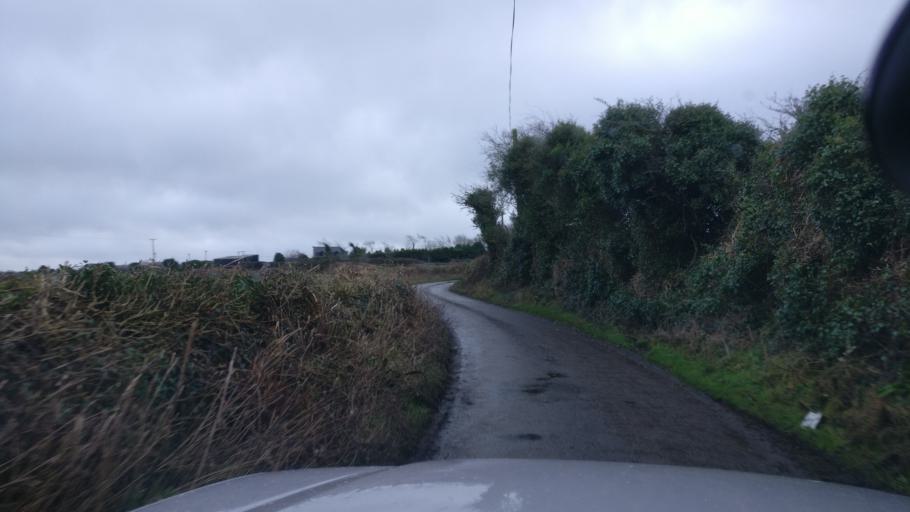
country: IE
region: Connaught
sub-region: County Galway
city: Loughrea
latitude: 53.2050
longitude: -8.6747
